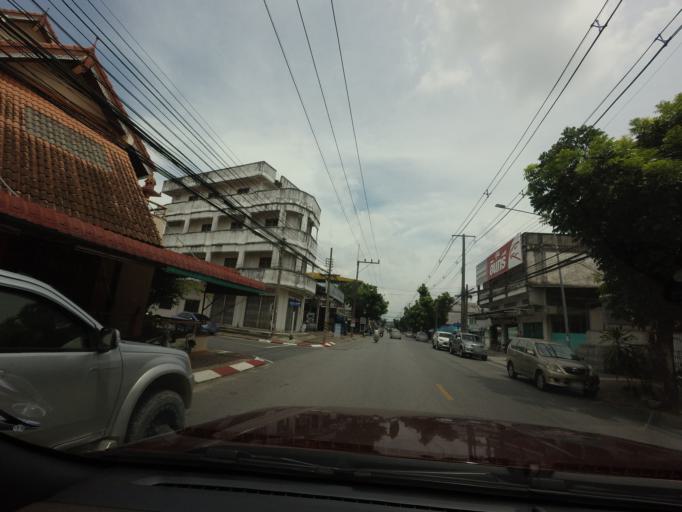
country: TH
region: Yala
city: Yala
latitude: 6.5451
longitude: 101.2913
